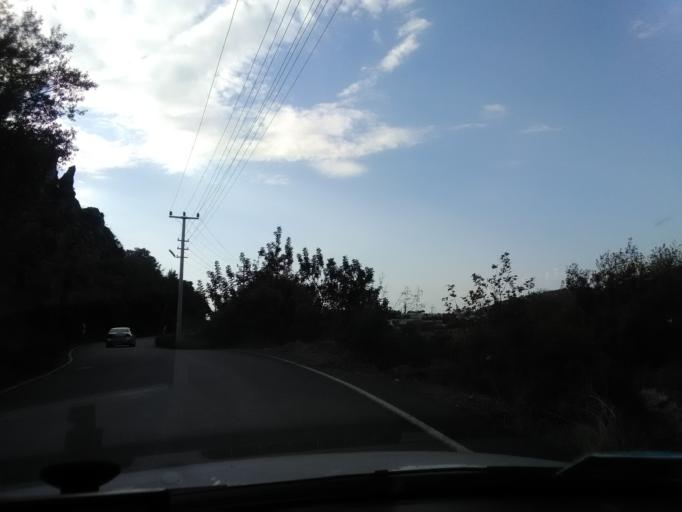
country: TR
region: Antalya
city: Gazipasa
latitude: 36.2751
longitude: 32.3521
